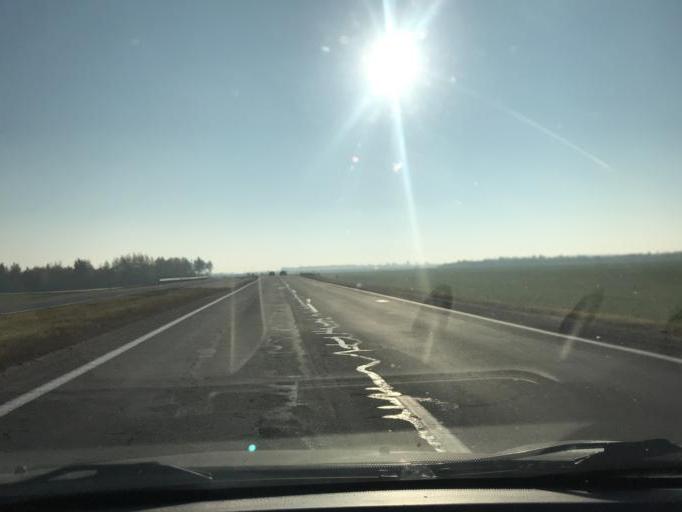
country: BY
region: Minsk
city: Dukora
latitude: 53.6469
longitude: 27.9819
